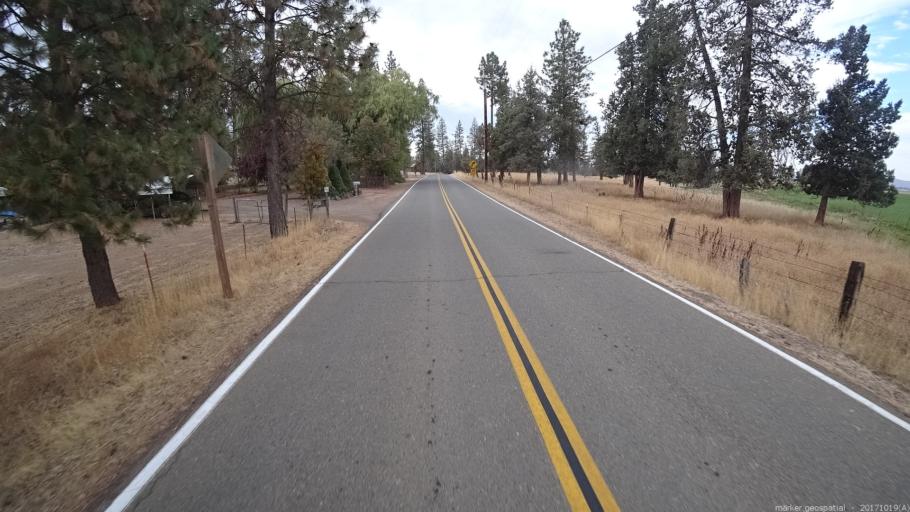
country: US
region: California
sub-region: Shasta County
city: Burney
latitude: 41.0313
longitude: -121.3850
